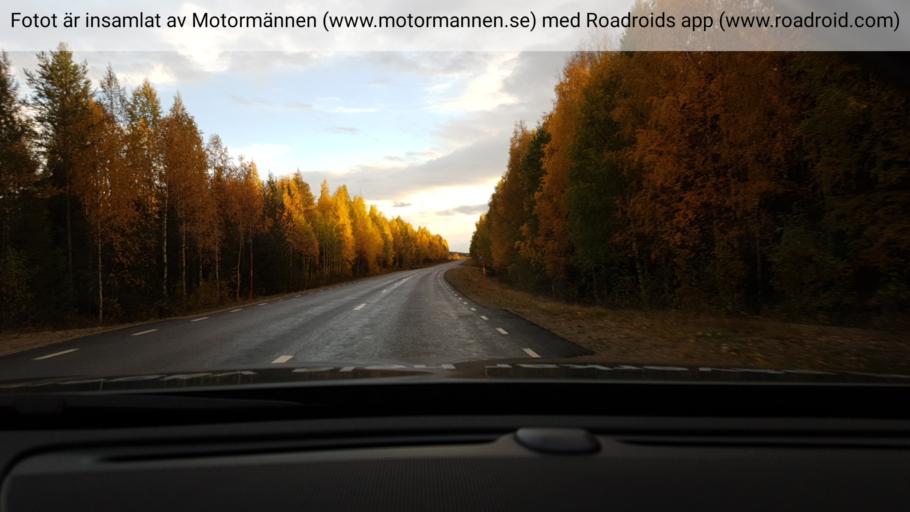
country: SE
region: Norrbotten
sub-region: Overkalix Kommun
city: OEverkalix
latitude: 66.5820
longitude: 22.7578
